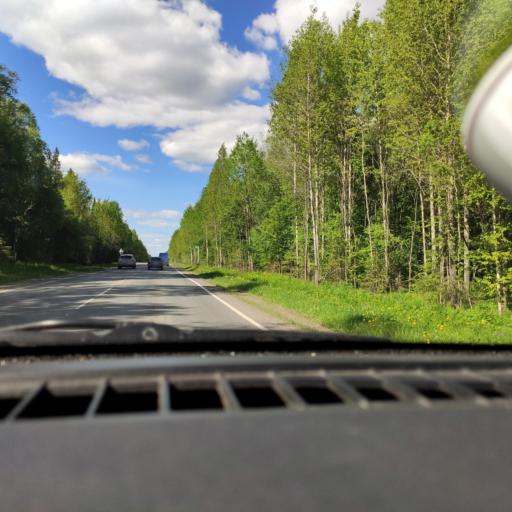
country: RU
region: Perm
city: Polazna
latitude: 58.2801
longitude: 56.1651
